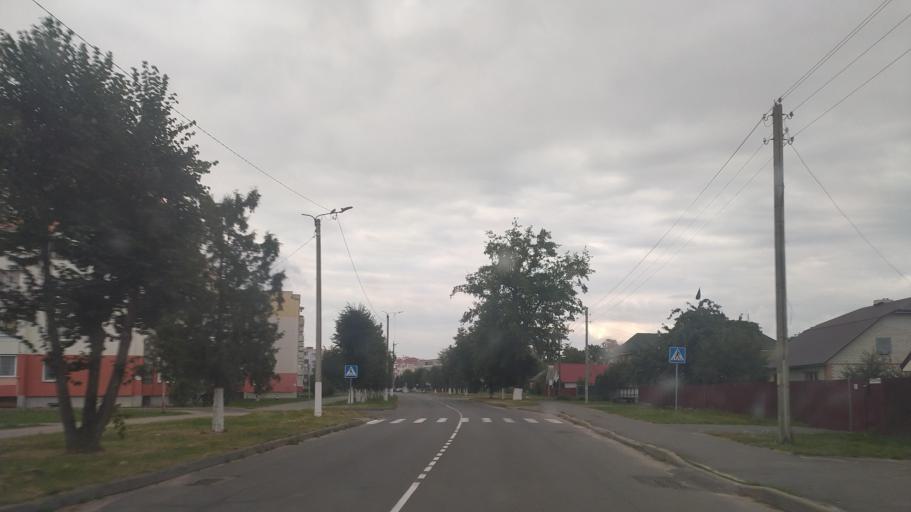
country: BY
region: Brest
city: Byaroza
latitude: 52.5301
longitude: 24.9870
